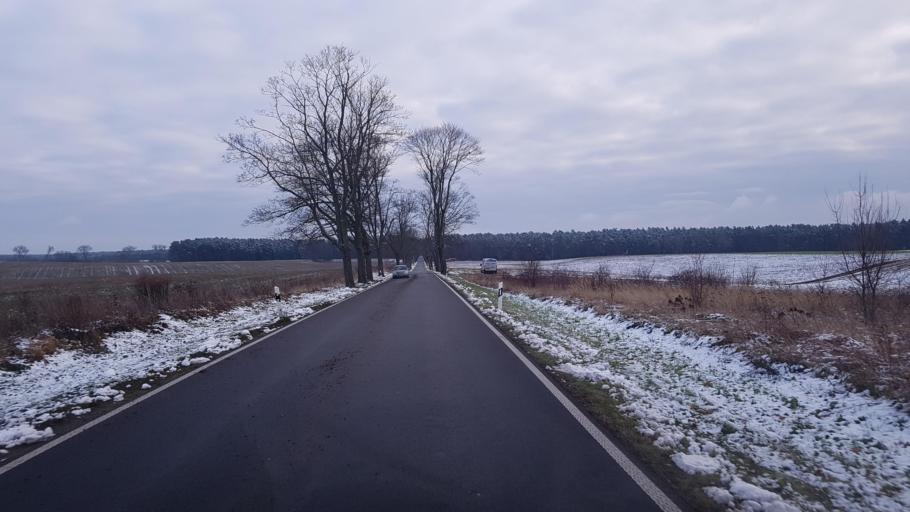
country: DE
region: Brandenburg
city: Strausberg
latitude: 52.5631
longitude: 13.9031
